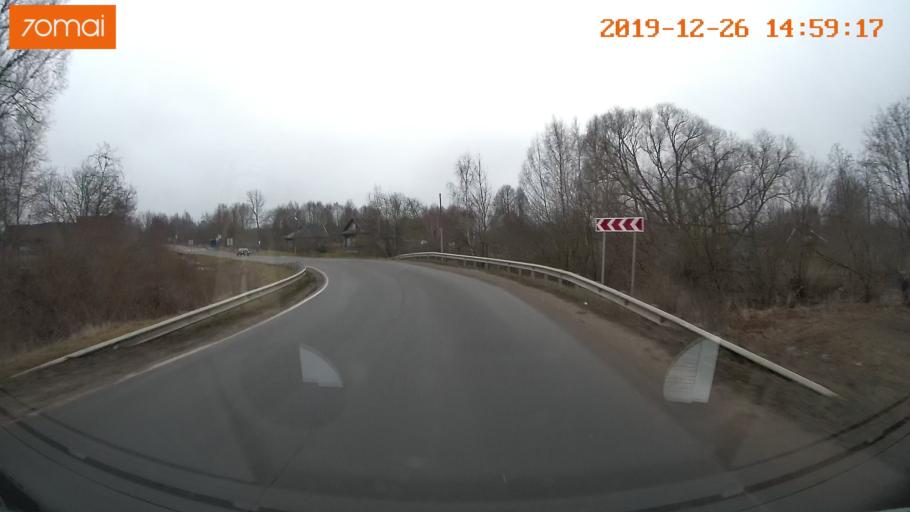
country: RU
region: Jaroslavl
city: Rybinsk
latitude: 58.2604
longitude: 38.8475
